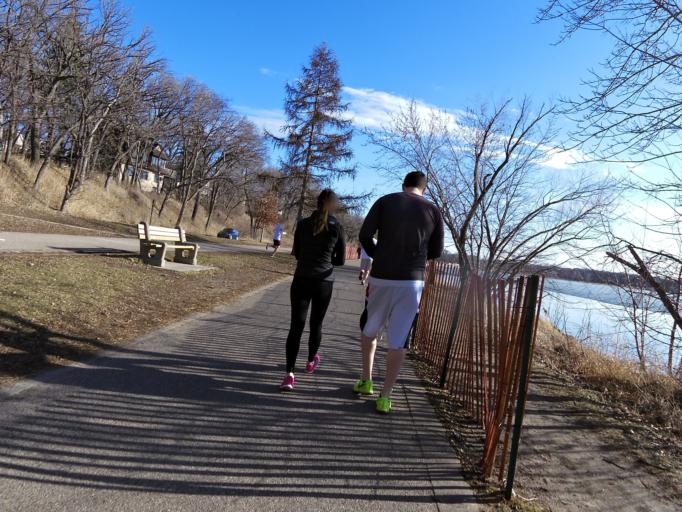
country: US
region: Minnesota
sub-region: Hennepin County
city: Saint Louis Park
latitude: 44.9418
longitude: -93.3039
